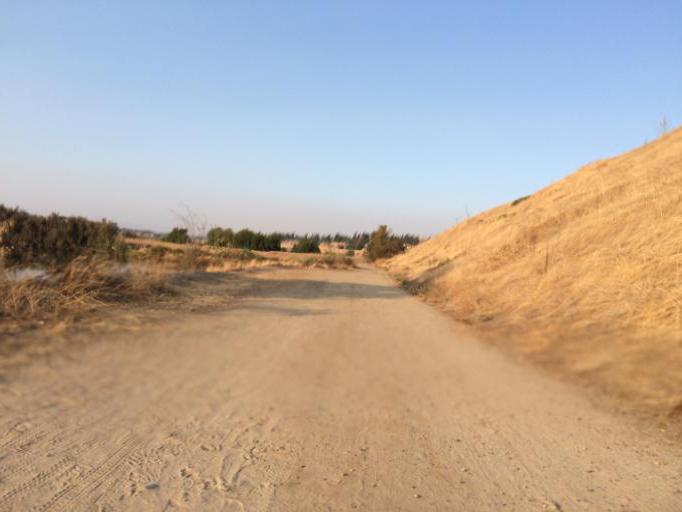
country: US
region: California
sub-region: Fresno County
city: Clovis
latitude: 36.8524
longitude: -119.8101
